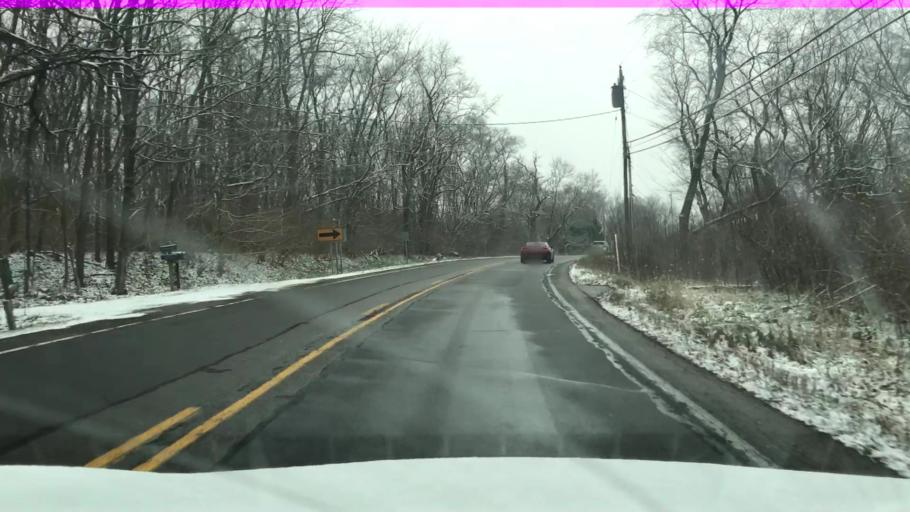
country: US
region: Indiana
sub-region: Delaware County
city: Daleville
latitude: 40.1521
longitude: -85.5345
